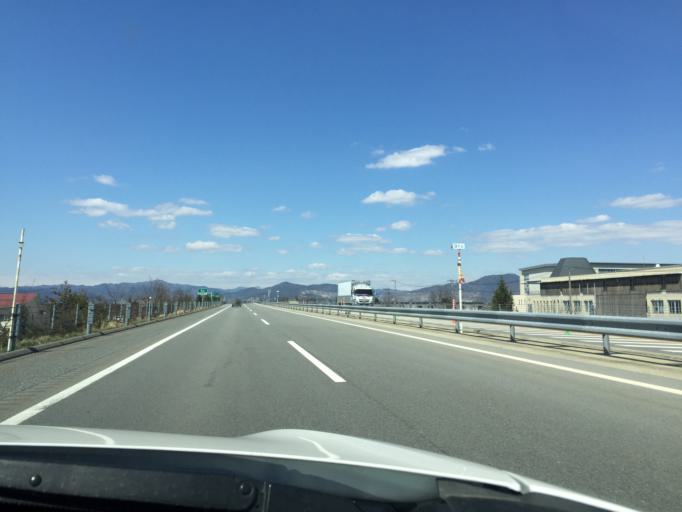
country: JP
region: Yamagata
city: Takahata
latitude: 37.9931
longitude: 140.1560
